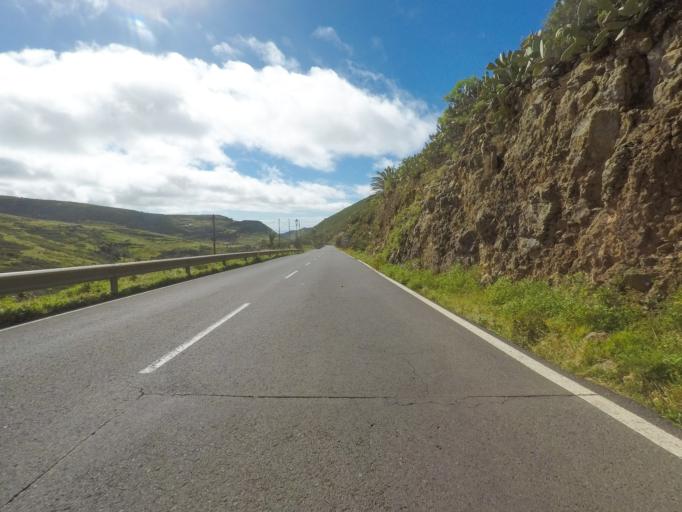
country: ES
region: Canary Islands
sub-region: Provincia de Santa Cruz de Tenerife
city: Vallehermosa
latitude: 28.1394
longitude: -17.3135
